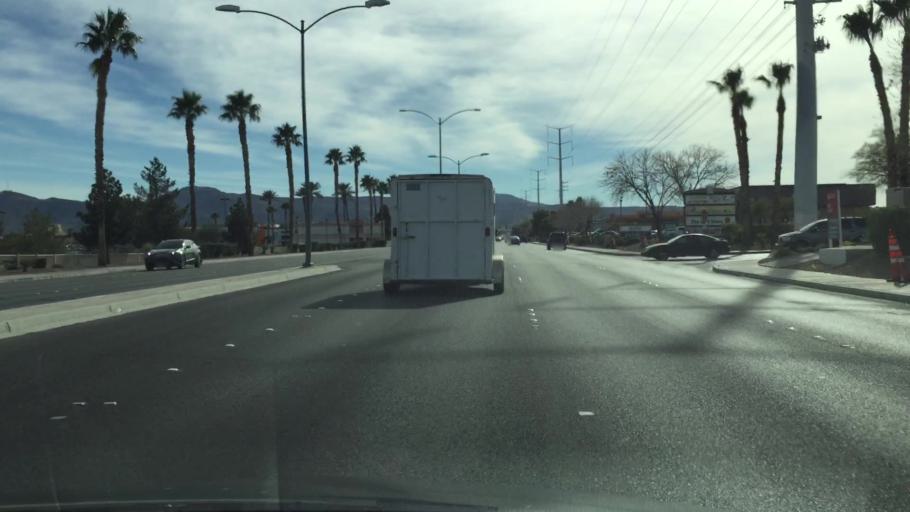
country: US
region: Nevada
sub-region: Clark County
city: Whitney
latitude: 36.0676
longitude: -115.0462
